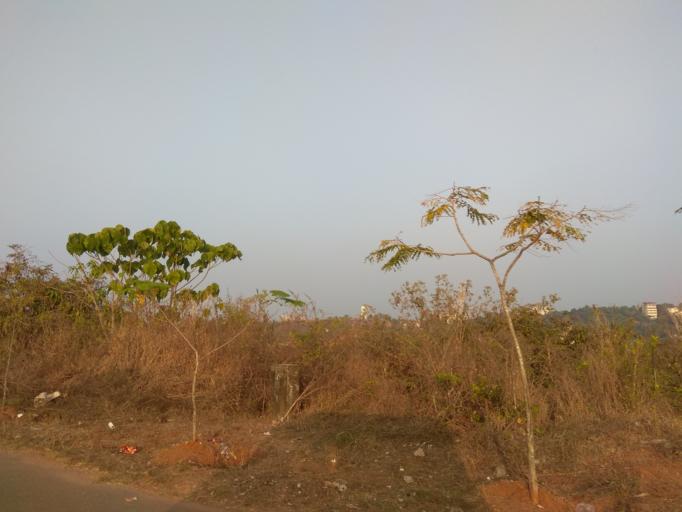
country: IN
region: Karnataka
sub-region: Dakshina Kannada
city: Mangalore
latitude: 12.9151
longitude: 74.8594
